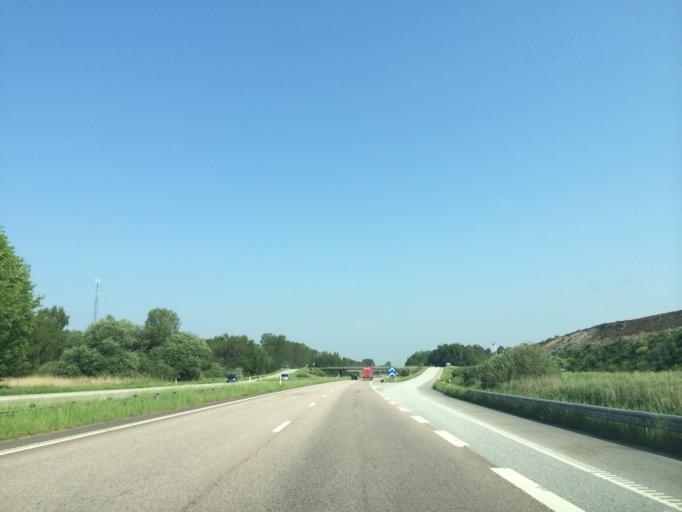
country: SE
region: Skane
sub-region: Kavlinge Kommun
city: Hofterup
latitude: 55.8185
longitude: 12.9379
